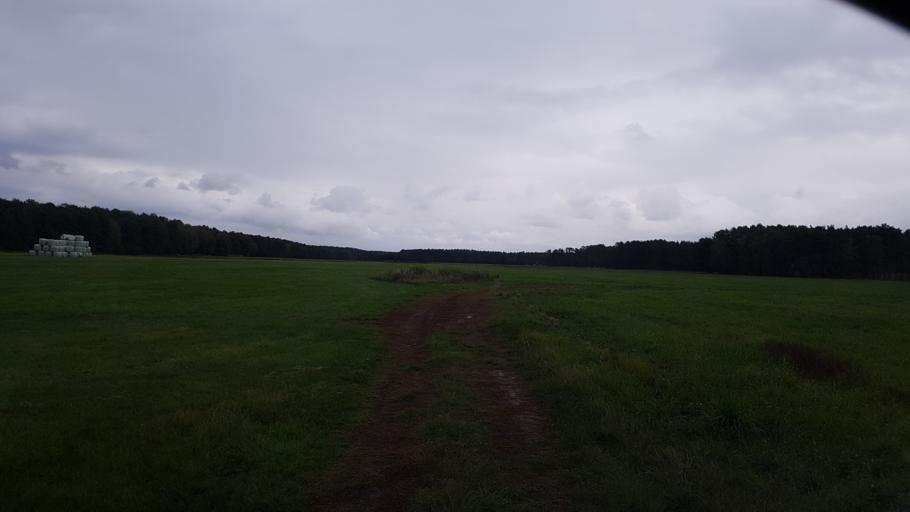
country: DE
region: Brandenburg
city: Finsterwalde
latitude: 51.5788
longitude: 13.6701
